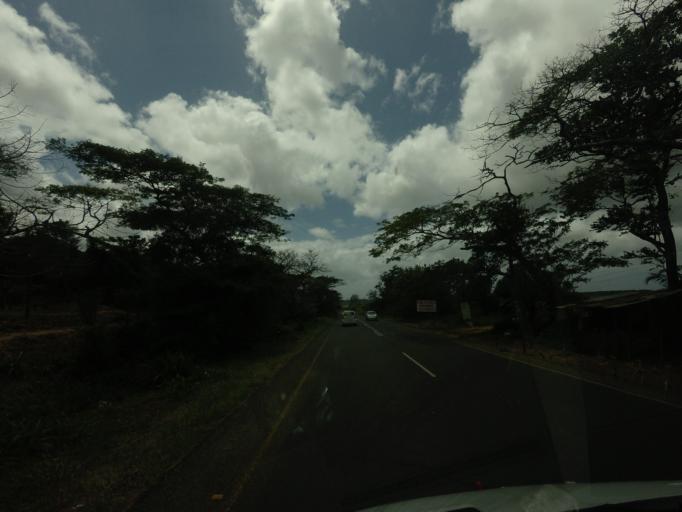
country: ZA
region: KwaZulu-Natal
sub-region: uMkhanyakude District Municipality
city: Mtubatuba
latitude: -28.3745
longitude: 32.3884
